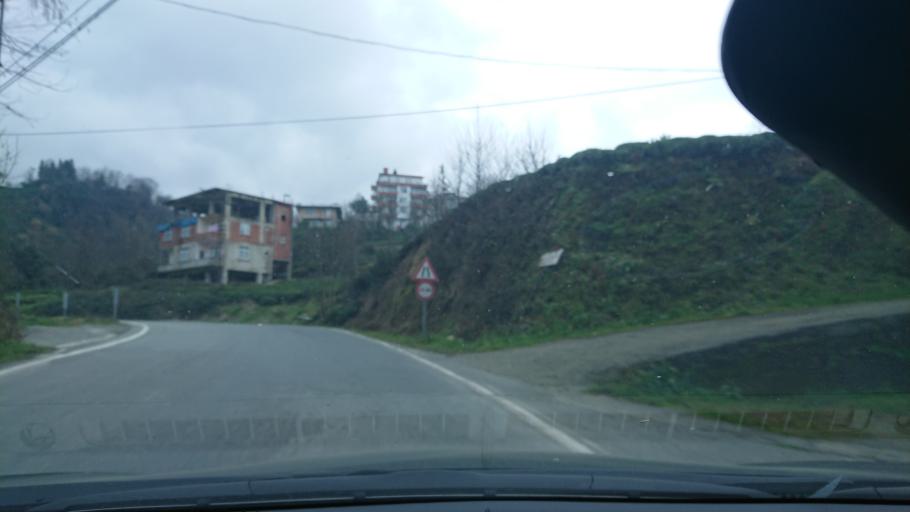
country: TR
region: Rize
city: Rize
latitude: 41.0235
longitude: 40.5021
